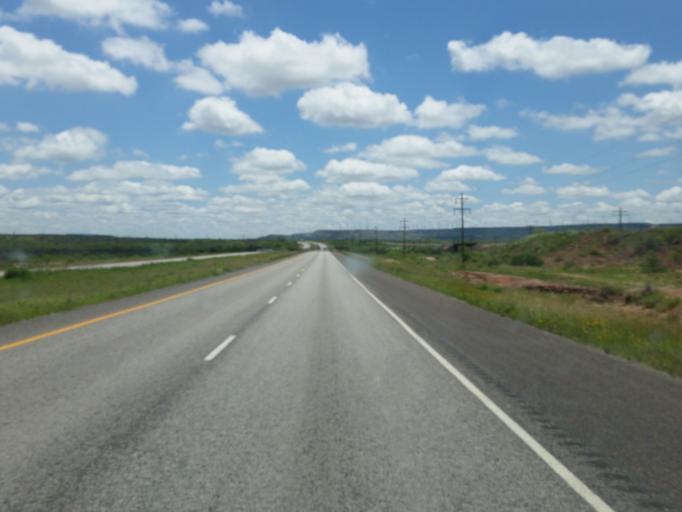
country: US
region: Texas
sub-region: Garza County
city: Post
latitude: 33.0093
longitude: -101.1708
